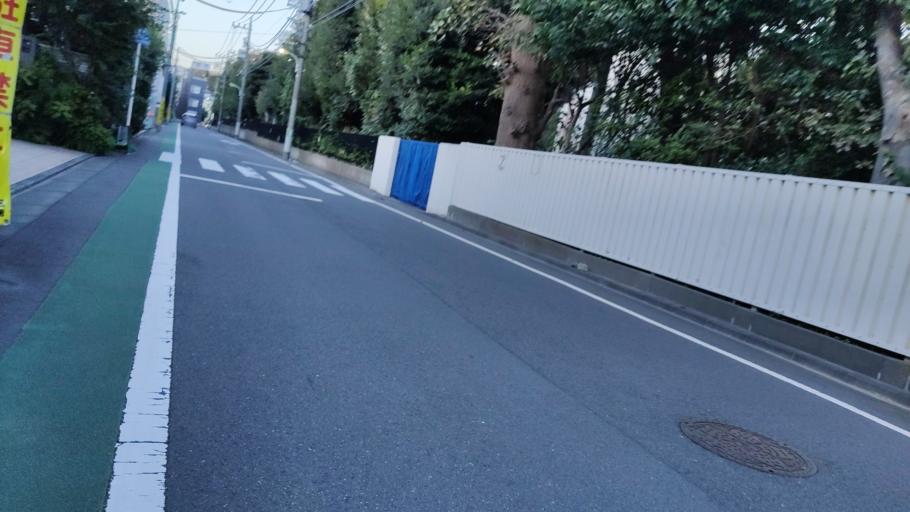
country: JP
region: Tokyo
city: Tokyo
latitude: 35.6544
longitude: 139.6802
